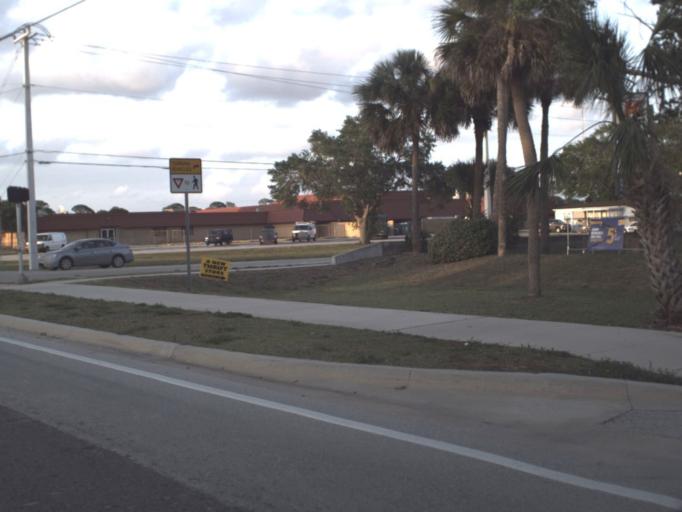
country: US
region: Florida
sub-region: Brevard County
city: Rockledge
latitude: 28.3238
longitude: -80.7426
